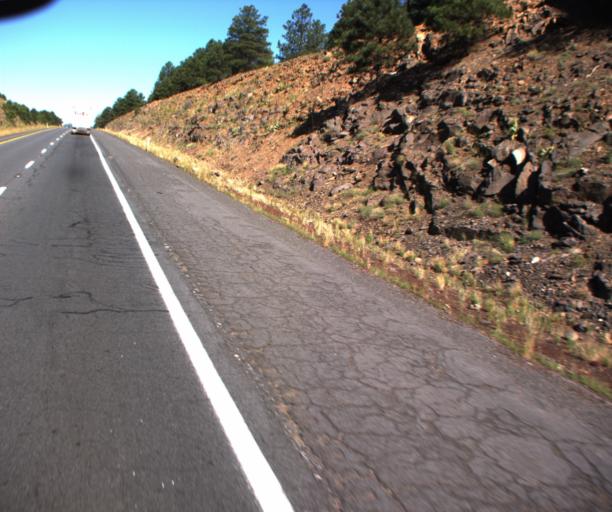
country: US
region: Arizona
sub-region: Coconino County
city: Parks
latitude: 35.2539
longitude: -112.0037
